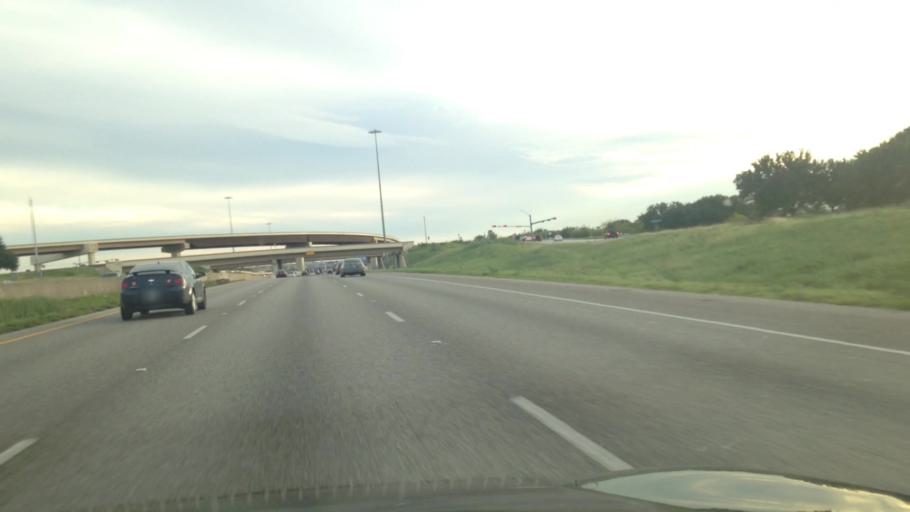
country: US
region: Texas
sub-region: Travis County
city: Onion Creek
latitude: 30.1149
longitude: -97.8062
